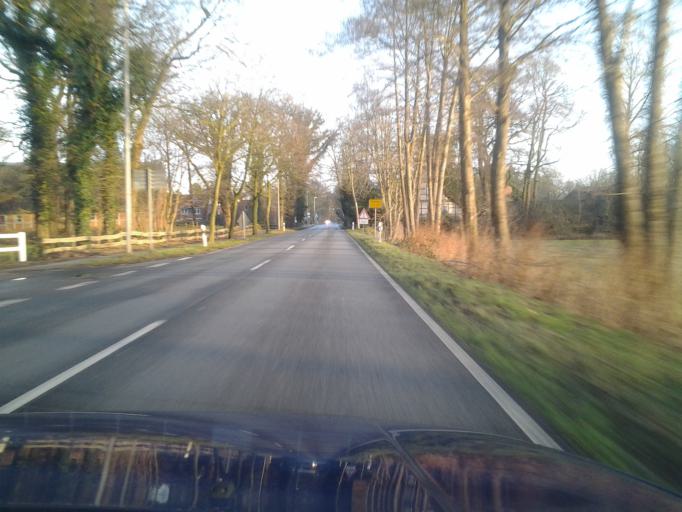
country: DE
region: Lower Saxony
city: Lilienthal
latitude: 53.1730
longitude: 8.8975
